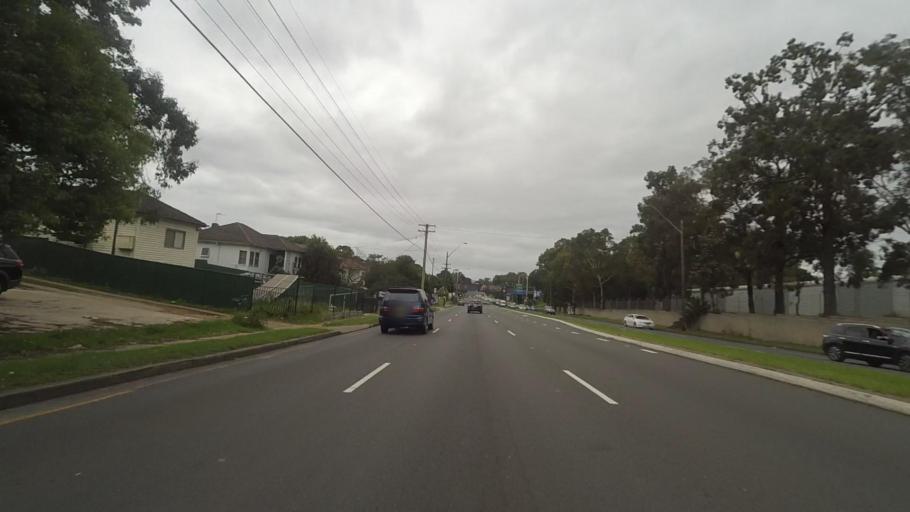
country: AU
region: New South Wales
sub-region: Auburn
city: Berala
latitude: -33.8866
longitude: 151.0396
